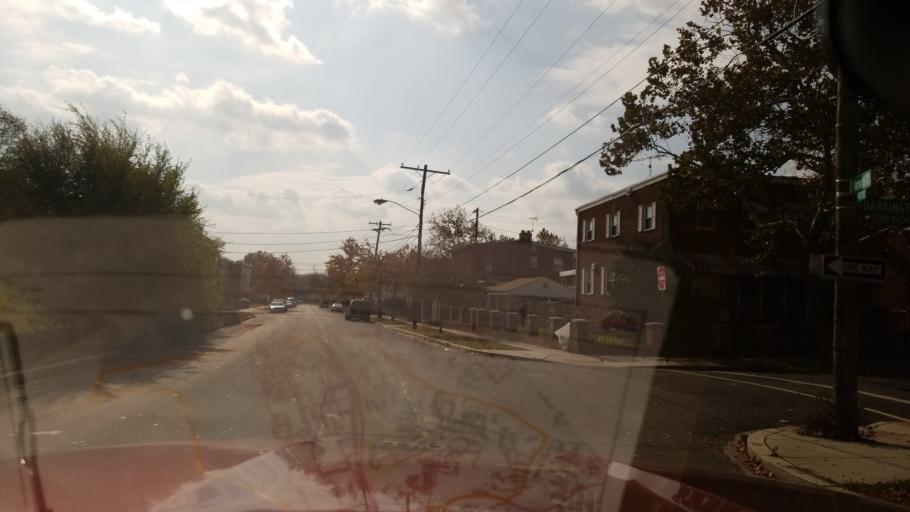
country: US
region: Maryland
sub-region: Prince George's County
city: Glassmanor
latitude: 38.8263
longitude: -76.9972
